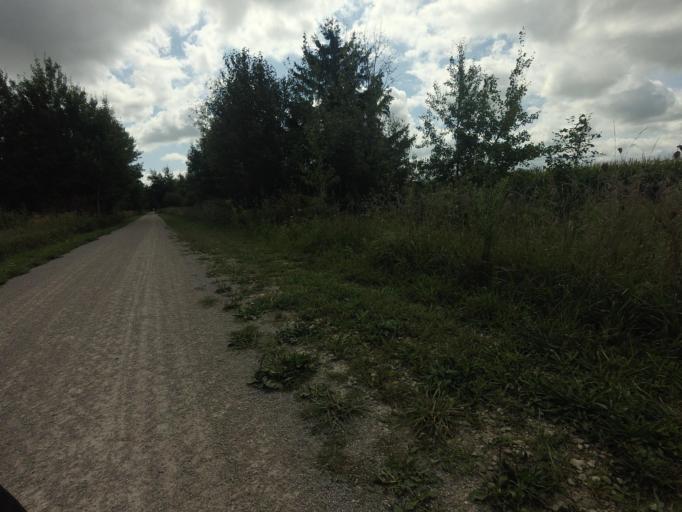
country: CA
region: Ontario
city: Huron East
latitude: 43.6150
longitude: -81.1417
